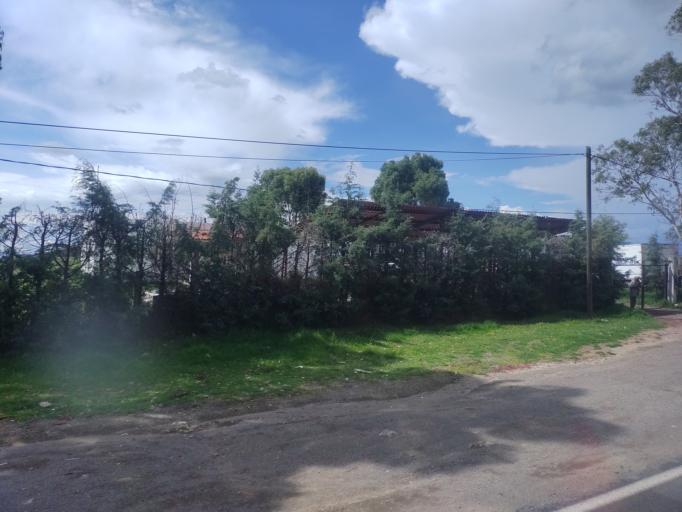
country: MX
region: Mexico
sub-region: Aculco
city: El Colorado
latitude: 20.0962
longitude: -99.7512
